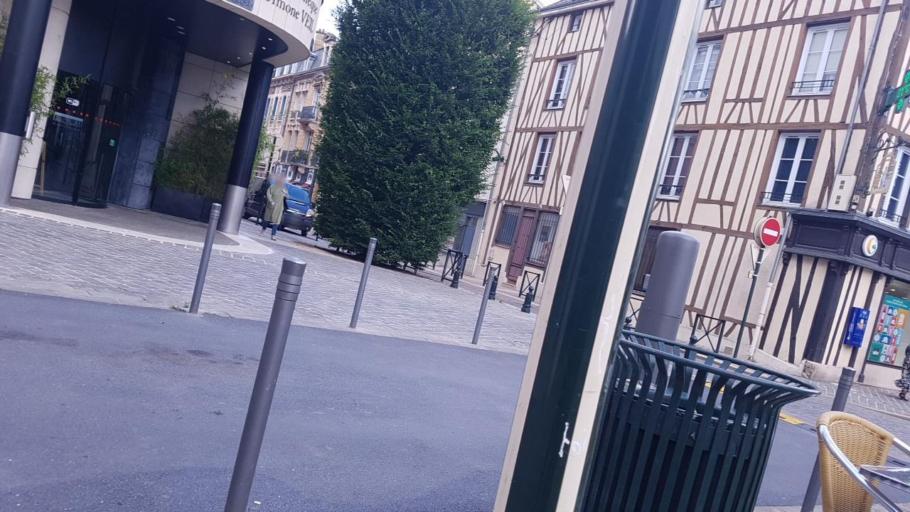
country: FR
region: Champagne-Ardenne
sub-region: Departement de la Marne
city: Epernay
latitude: 49.0432
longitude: 3.9536
